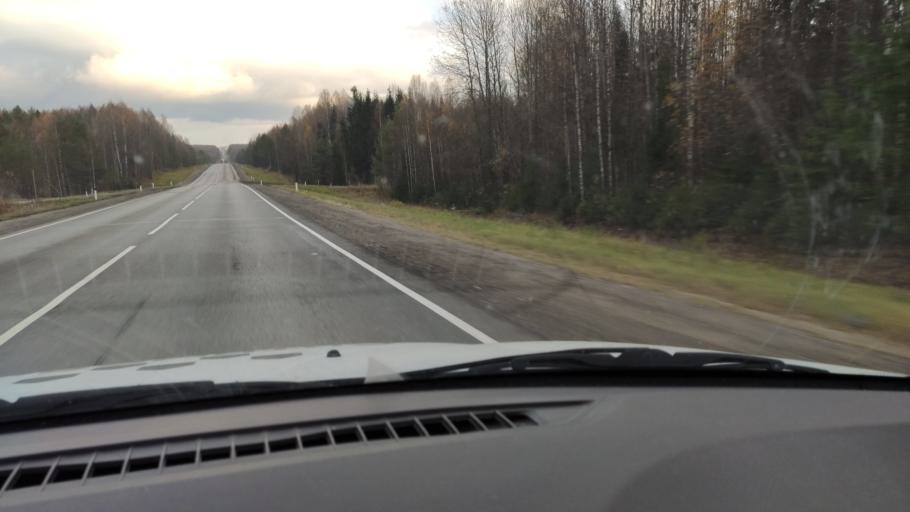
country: RU
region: Kirov
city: Chernaya Kholunitsa
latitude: 58.8120
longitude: 51.8320
